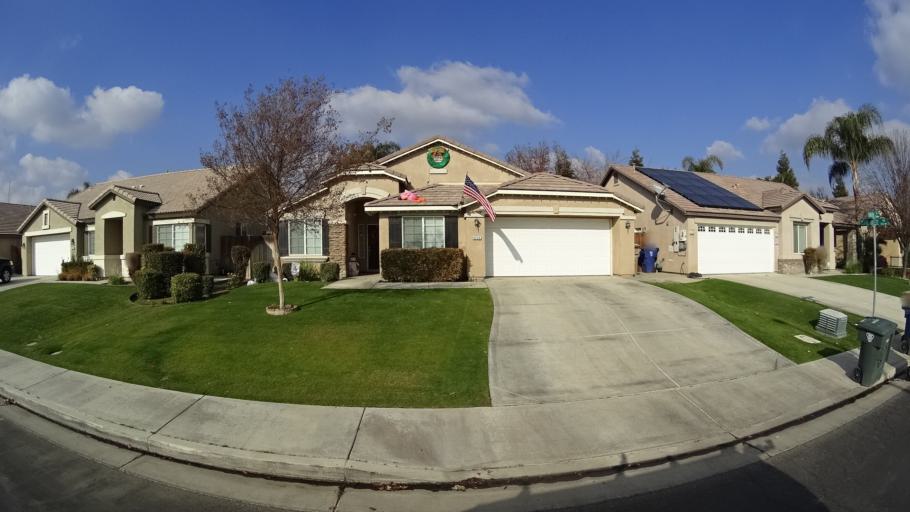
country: US
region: California
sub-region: Kern County
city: Greenacres
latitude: 35.3059
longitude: -119.1069
